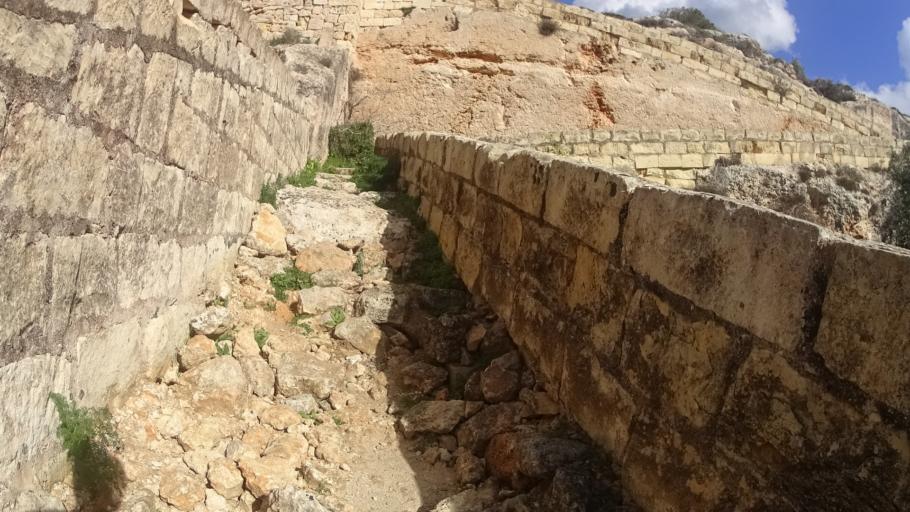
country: MT
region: L-Imgarr
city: Imgarr
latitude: 35.9036
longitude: 14.3788
